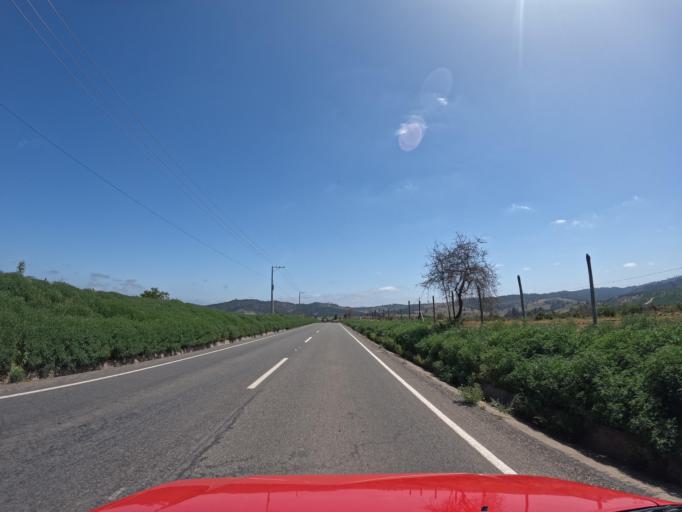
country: CL
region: O'Higgins
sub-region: Provincia de Colchagua
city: Santa Cruz
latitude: -34.6549
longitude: -71.8606
